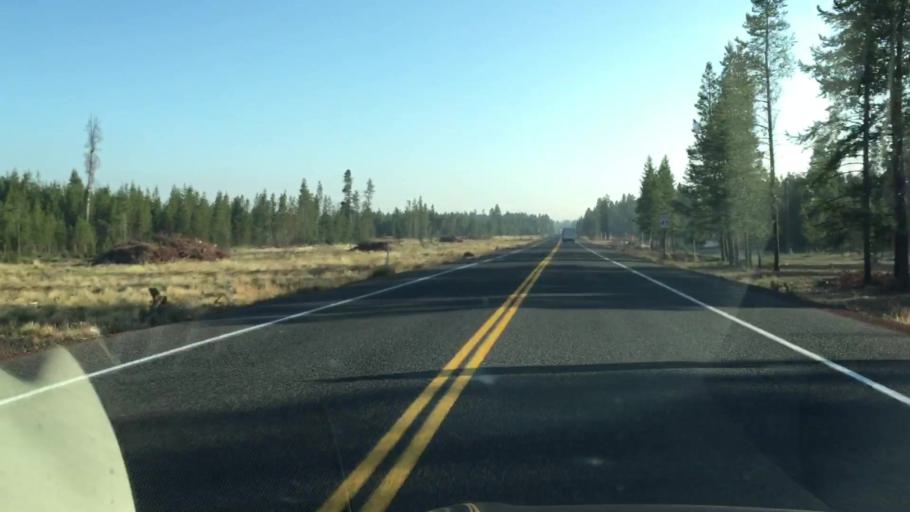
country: US
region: Oregon
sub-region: Deschutes County
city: La Pine
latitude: 43.4474
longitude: -121.7069
